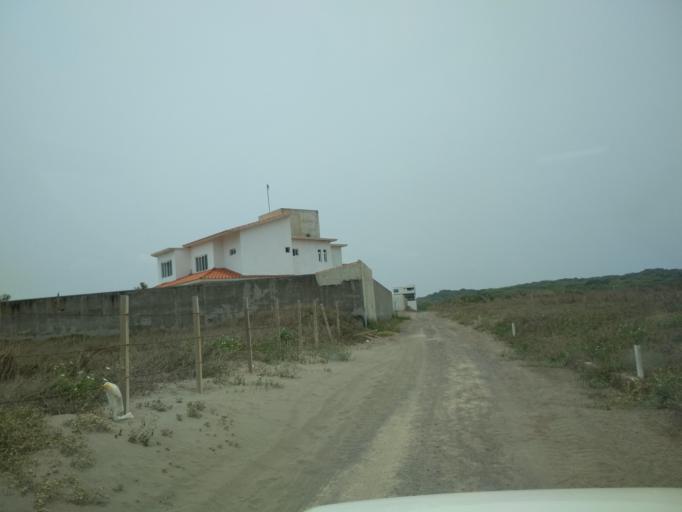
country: MX
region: Veracruz
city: Anton Lizardo
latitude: 19.0576
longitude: -96.0427
